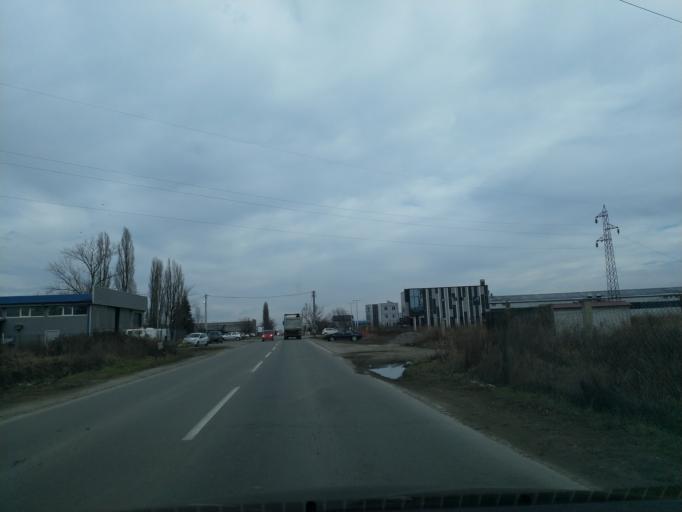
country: RS
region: Central Serbia
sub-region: Belgrade
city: Zvezdara
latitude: 44.7359
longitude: 20.5904
